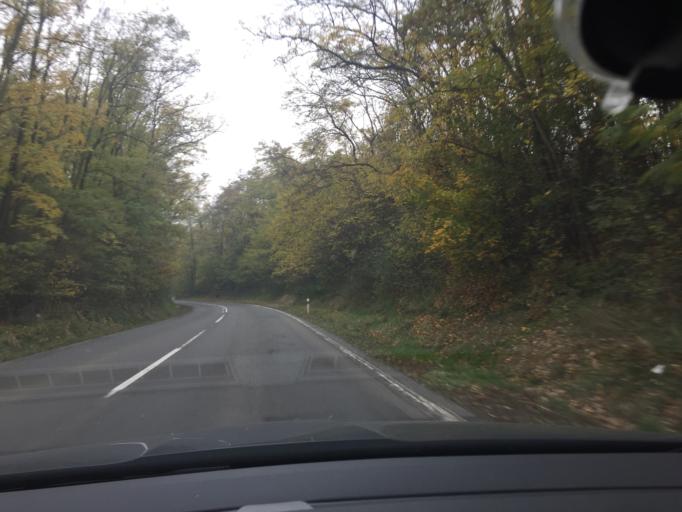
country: SK
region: Banskobystricky
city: Velky Krtis
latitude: 48.2625
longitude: 19.4280
